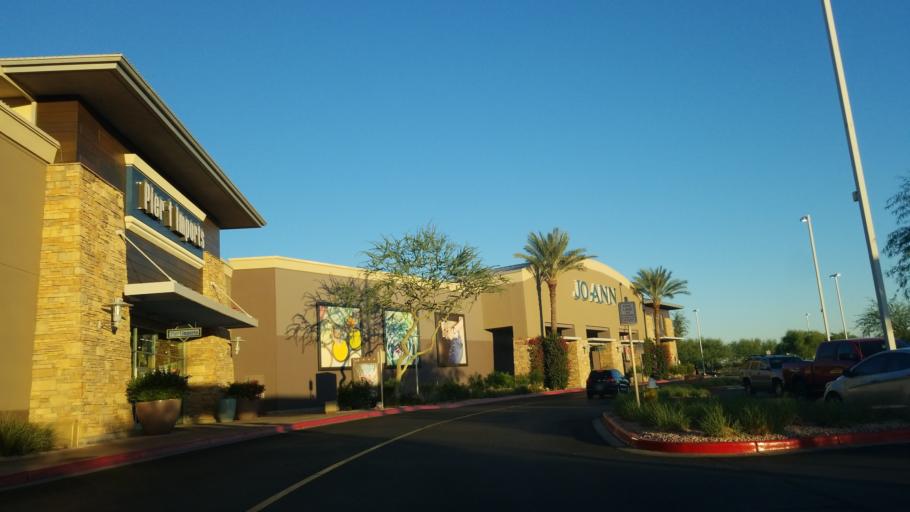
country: US
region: Arizona
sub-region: Maricopa County
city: Paradise Valley
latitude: 33.6778
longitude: -111.9710
